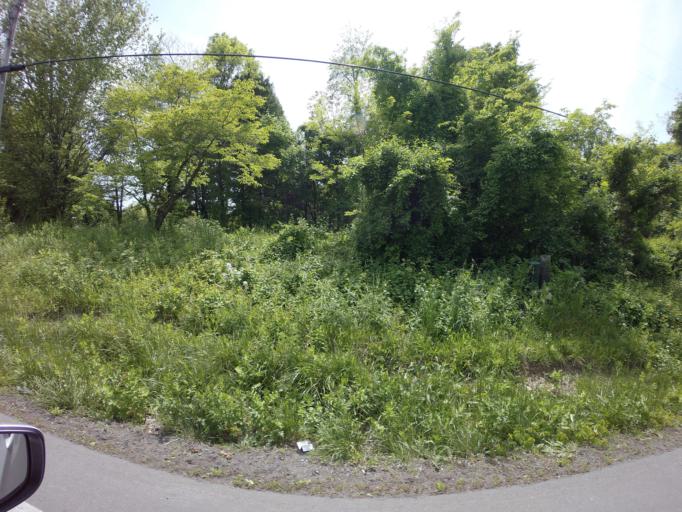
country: US
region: Maryland
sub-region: Frederick County
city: Woodsboro
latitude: 39.5380
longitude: -77.3007
